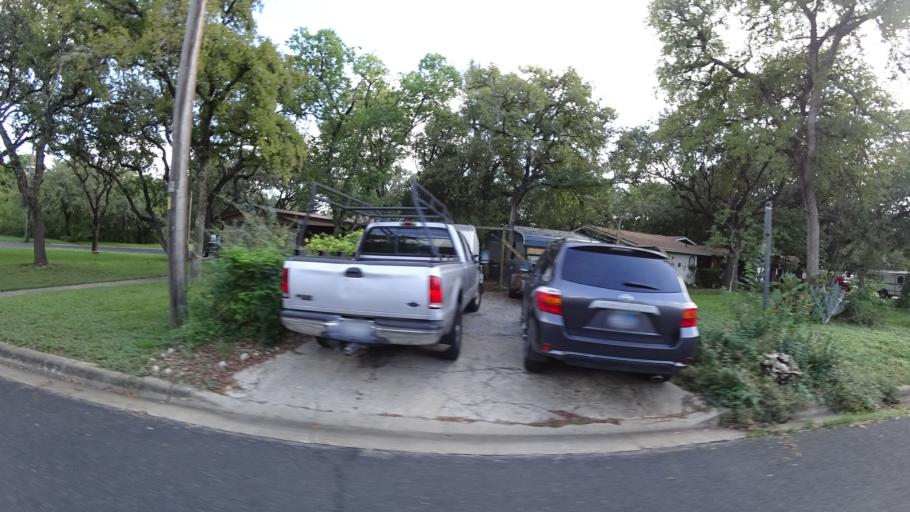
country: US
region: Texas
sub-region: Travis County
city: Rollingwood
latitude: 30.2110
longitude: -97.7904
